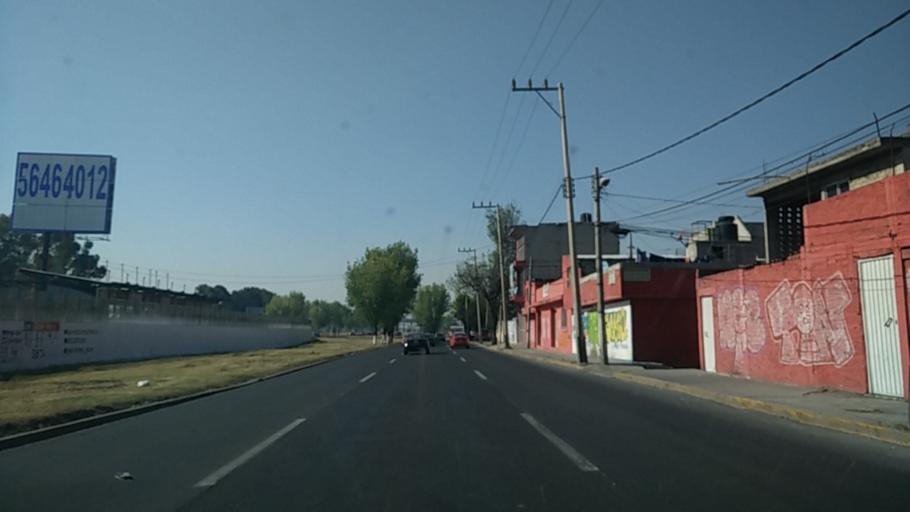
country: MX
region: Mexico
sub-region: Atenco
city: Colonia el Salado
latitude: 19.6010
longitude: -99.0163
